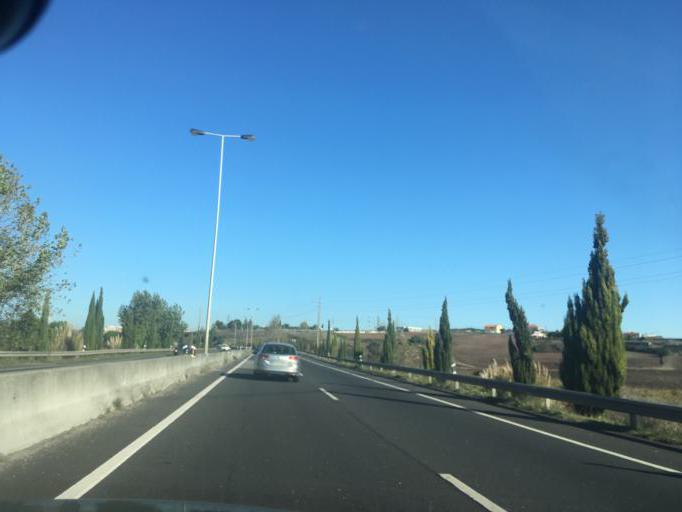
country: PT
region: Lisbon
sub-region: Oeiras
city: Porto Salvo
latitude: 38.7271
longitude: -9.2961
